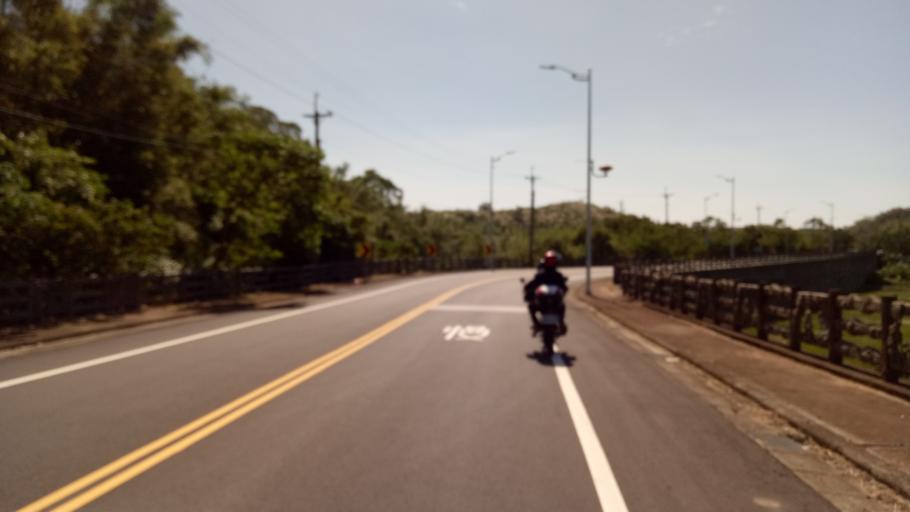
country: TW
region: Taiwan
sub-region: Hsinchu
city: Hsinchu
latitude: 24.7223
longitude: 120.9259
